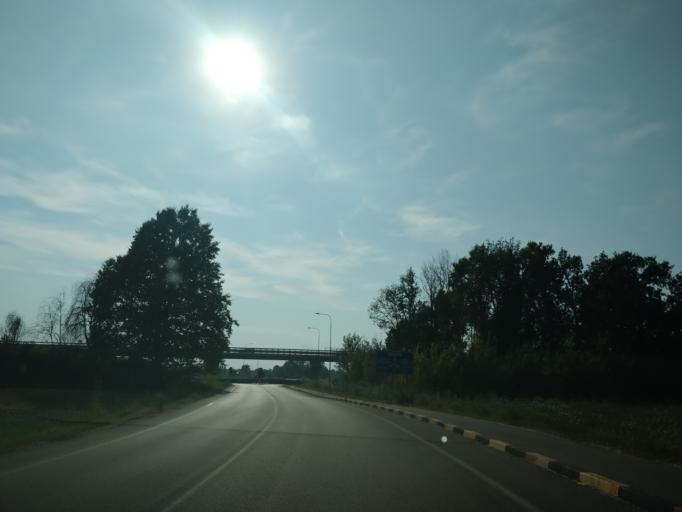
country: IT
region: Emilia-Romagna
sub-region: Provincia di Bologna
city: Progresso
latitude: 44.5621
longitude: 11.3459
